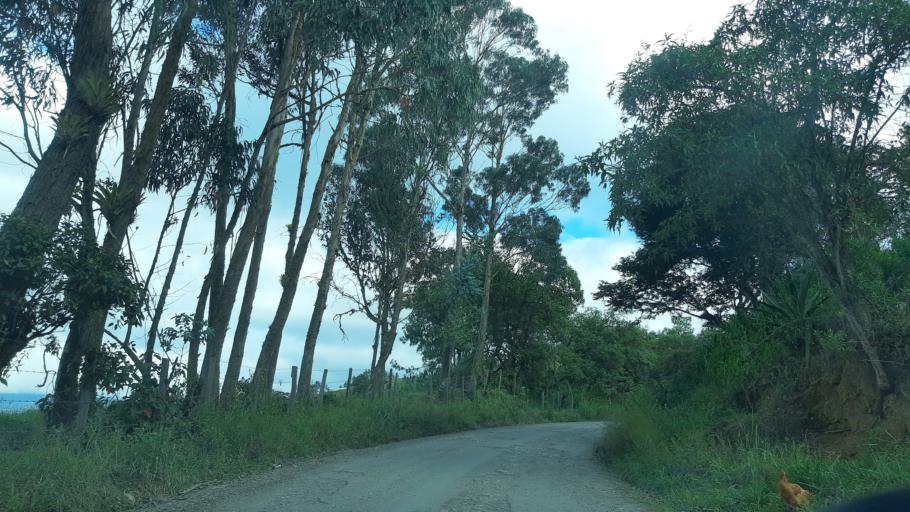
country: CO
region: Cundinamarca
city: Tenza
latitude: 5.0444
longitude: -73.4177
